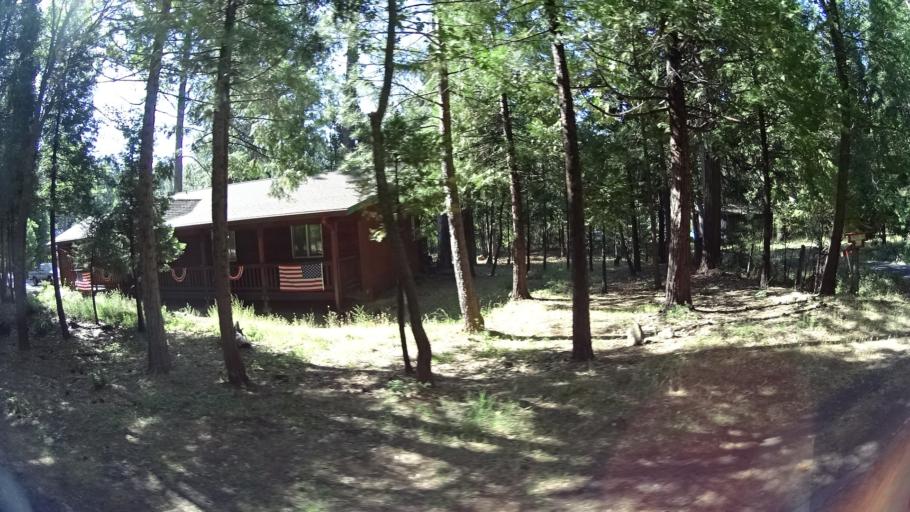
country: US
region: California
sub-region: Calaveras County
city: Arnold
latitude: 38.2372
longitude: -120.3696
